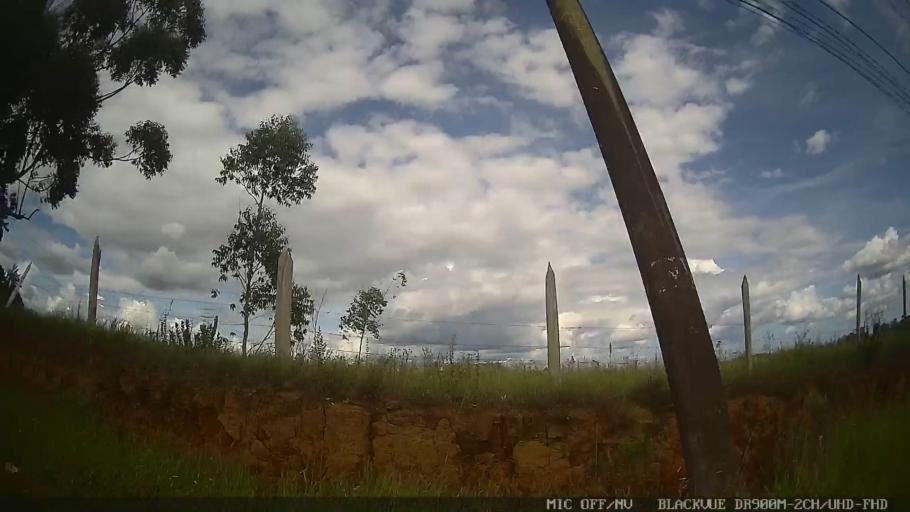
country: BR
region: Sao Paulo
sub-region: Mogi das Cruzes
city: Mogi das Cruzes
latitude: -23.6004
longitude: -46.2355
